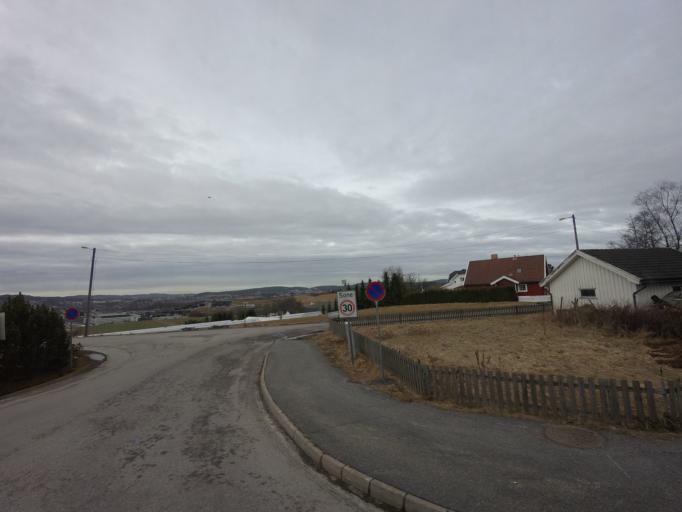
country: NO
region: Akershus
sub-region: Skedsmo
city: Lillestrom
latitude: 59.9829
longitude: 11.0510
